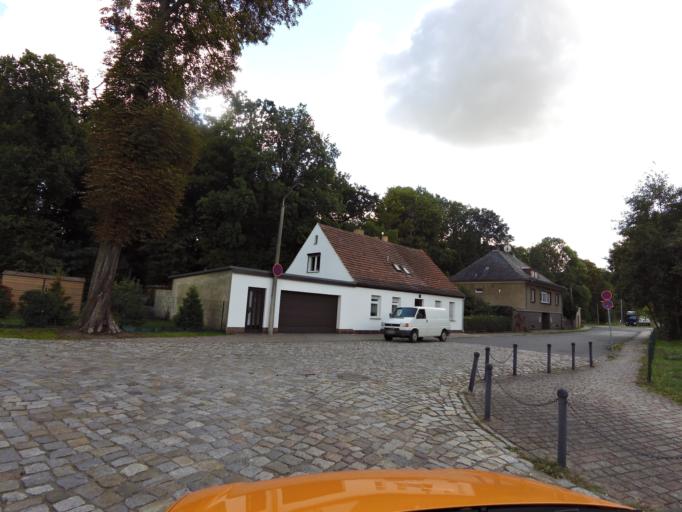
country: DE
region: Brandenburg
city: Luckenwalde
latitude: 52.0830
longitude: 13.1677
